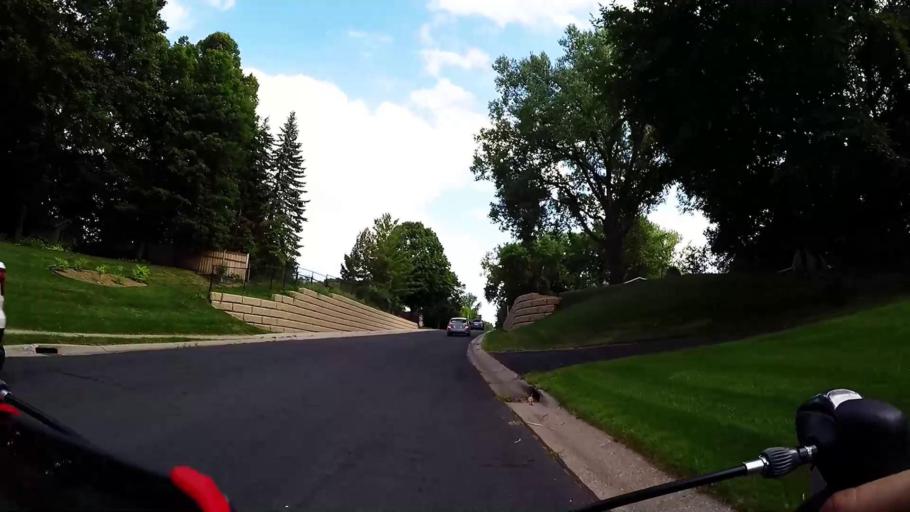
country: US
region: Minnesota
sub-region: Hennepin County
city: Minnetonka
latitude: 44.8878
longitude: -93.4908
